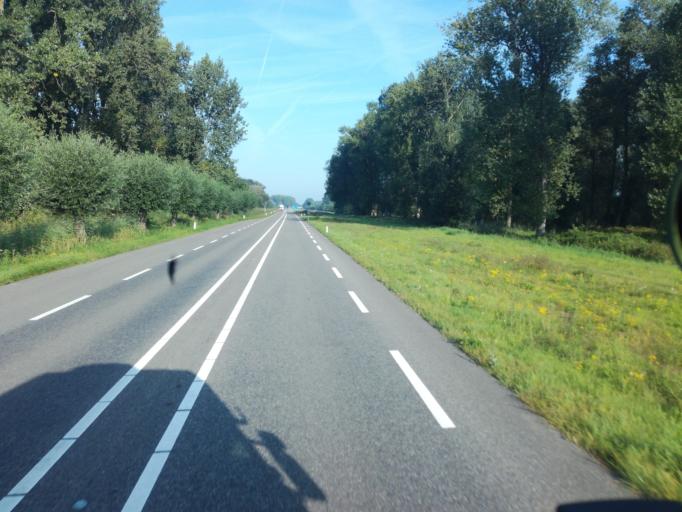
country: NL
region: North Brabant
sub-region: Gemeente Heusden
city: Heusden
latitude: 51.7138
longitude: 5.1501
